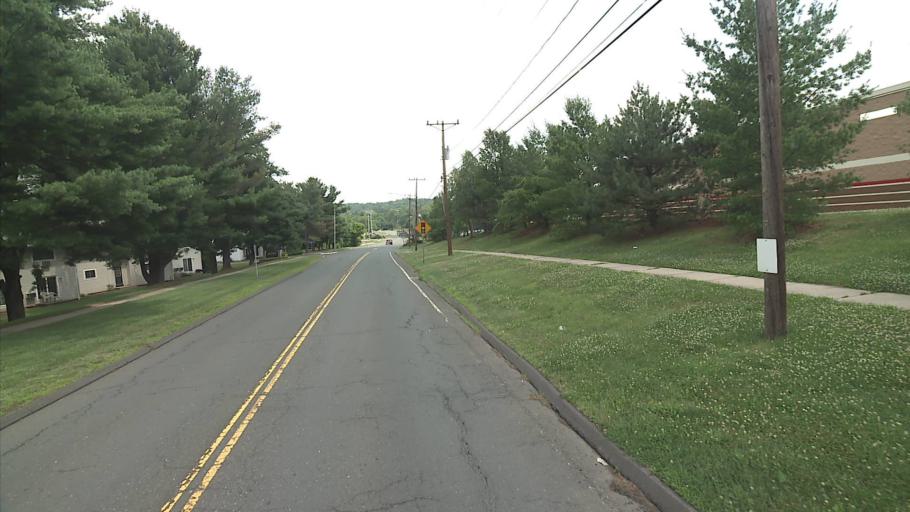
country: US
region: Connecticut
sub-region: Hartford County
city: Newington
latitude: 41.6618
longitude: -72.7251
